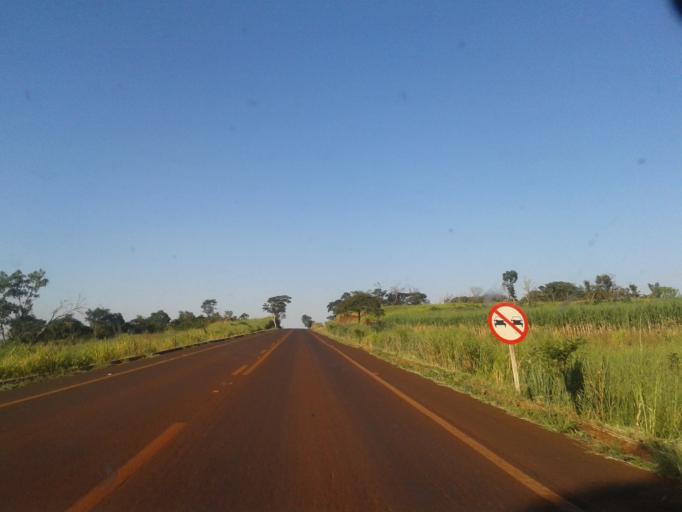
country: BR
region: Minas Gerais
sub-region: Capinopolis
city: Capinopolis
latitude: -18.6944
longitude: -49.6257
